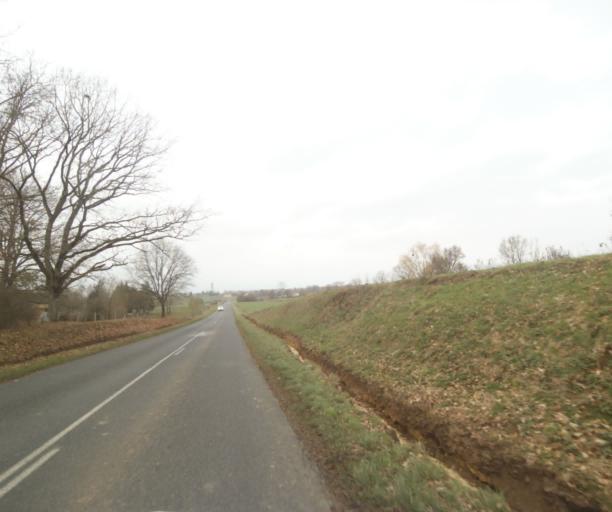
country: FR
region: Champagne-Ardenne
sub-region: Departement de la Marne
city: Pargny-sur-Saulx
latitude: 48.7405
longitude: 4.8526
